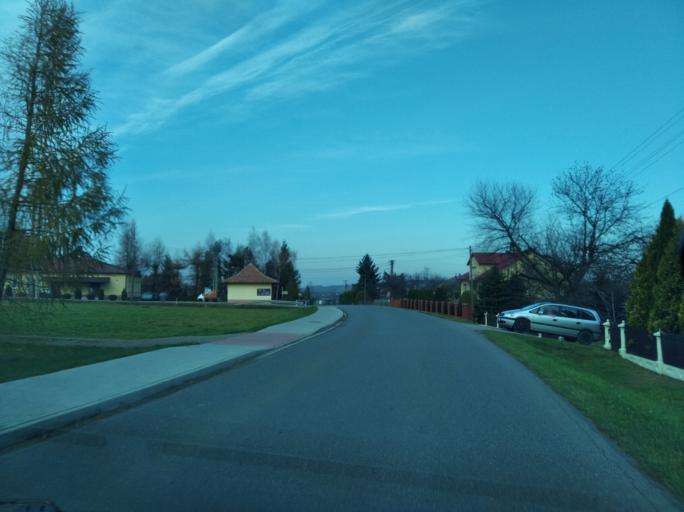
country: PL
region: Subcarpathian Voivodeship
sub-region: Powiat ropczycko-sedziszowski
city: Iwierzyce
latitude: 50.0051
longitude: 21.7554
